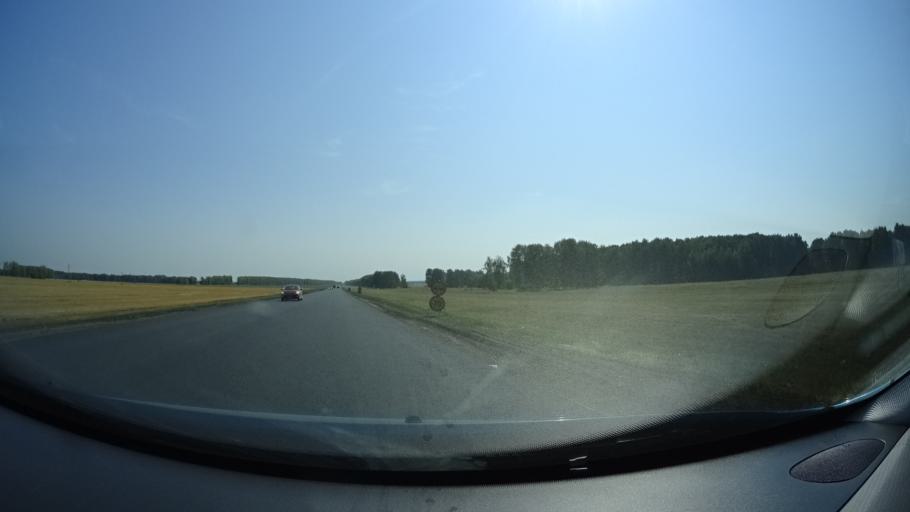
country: RU
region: Bashkortostan
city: Karmaskaly
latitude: 54.4013
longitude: 56.0908
